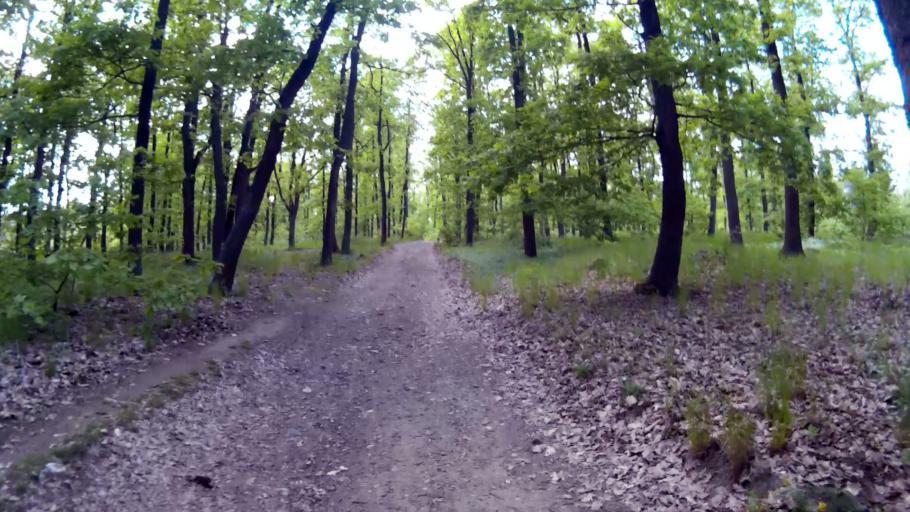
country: CZ
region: South Moravian
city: Troubsko
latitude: 49.1874
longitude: 16.5189
